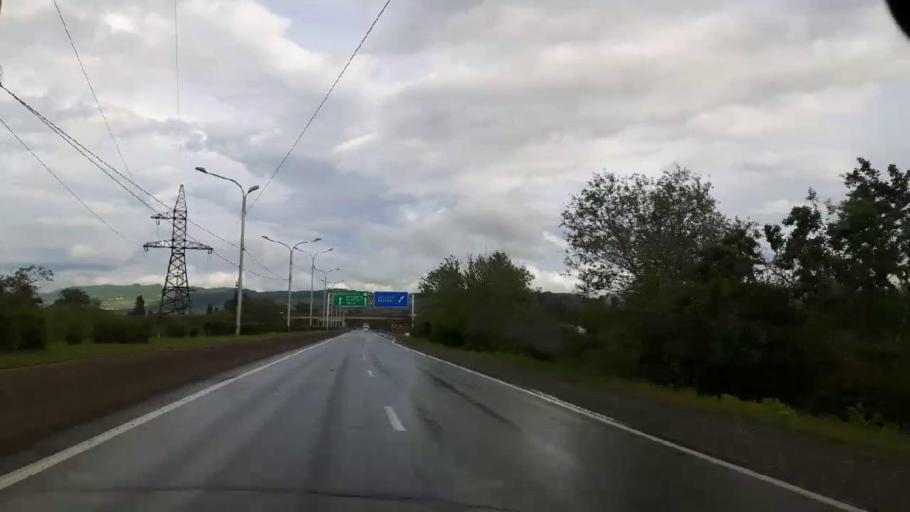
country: GE
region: Shida Kartli
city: Kaspi
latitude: 41.9148
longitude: 44.5571
